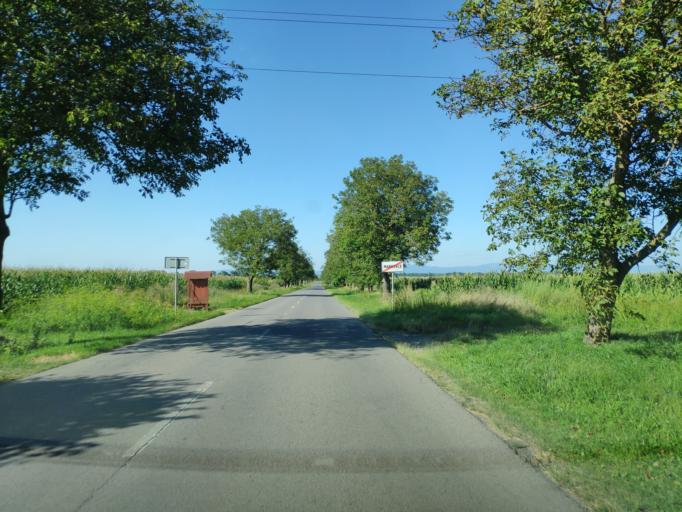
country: SK
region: Kosicky
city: Trebisov
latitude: 48.5970
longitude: 21.8466
